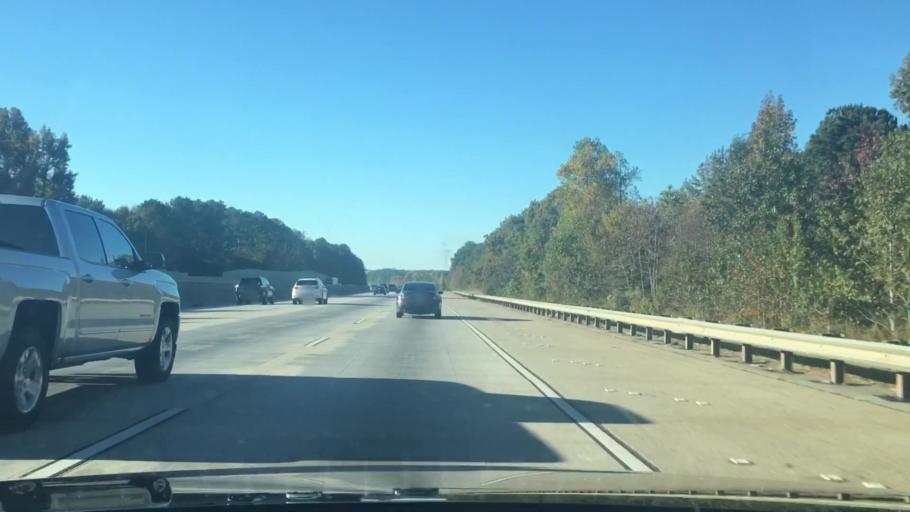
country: US
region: Georgia
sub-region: Fulton County
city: Palmetto
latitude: 33.4728
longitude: -84.6656
